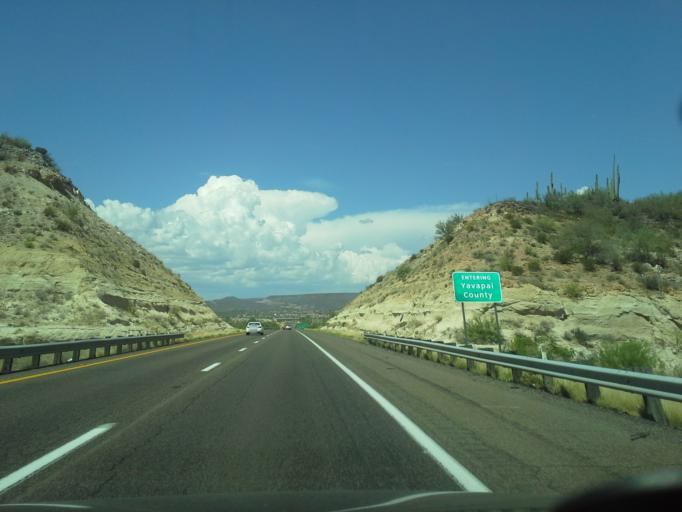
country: US
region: Arizona
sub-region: Yavapai County
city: Black Canyon City
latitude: 34.0447
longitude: -112.1456
